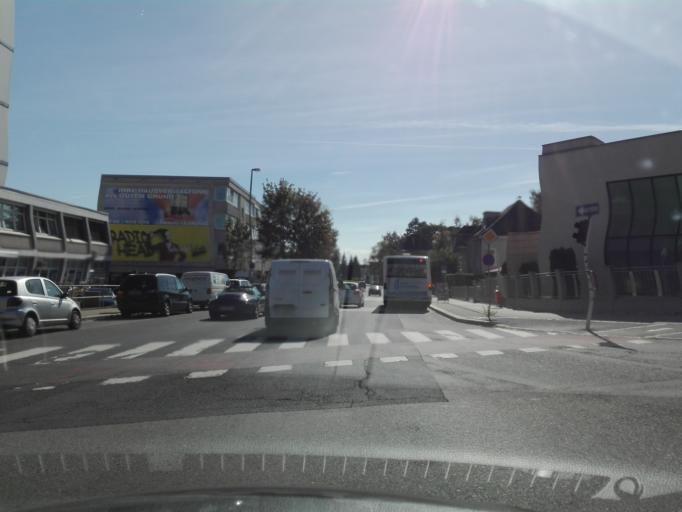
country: AT
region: Upper Austria
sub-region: Linz Stadt
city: Linz
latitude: 48.2759
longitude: 14.3114
